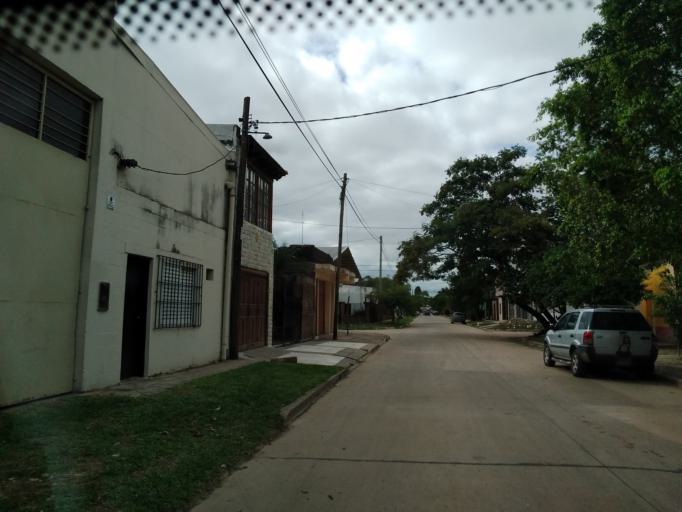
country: AR
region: Corrientes
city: Corrientes
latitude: -27.4757
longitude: -58.8091
